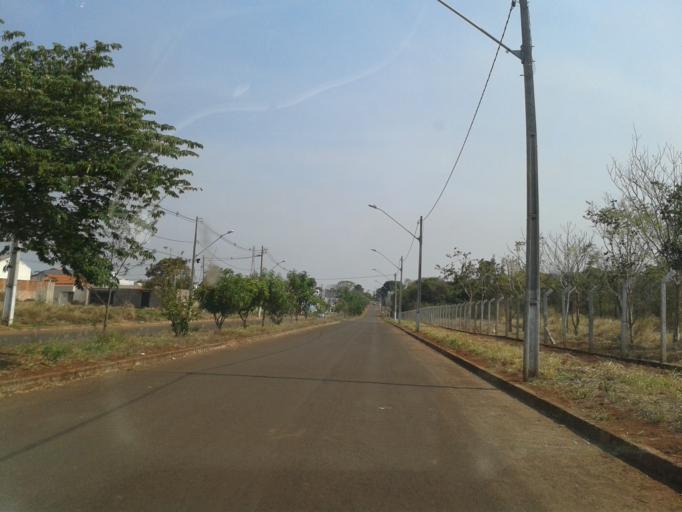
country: BR
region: Minas Gerais
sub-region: Ituiutaba
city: Ituiutaba
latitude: -18.9638
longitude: -49.4411
